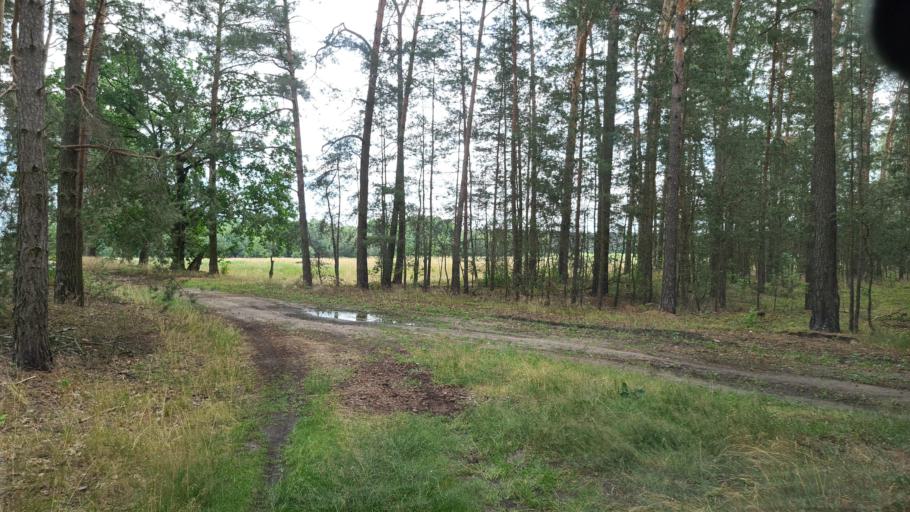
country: DE
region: Brandenburg
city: Crinitz
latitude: 51.7158
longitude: 13.8328
